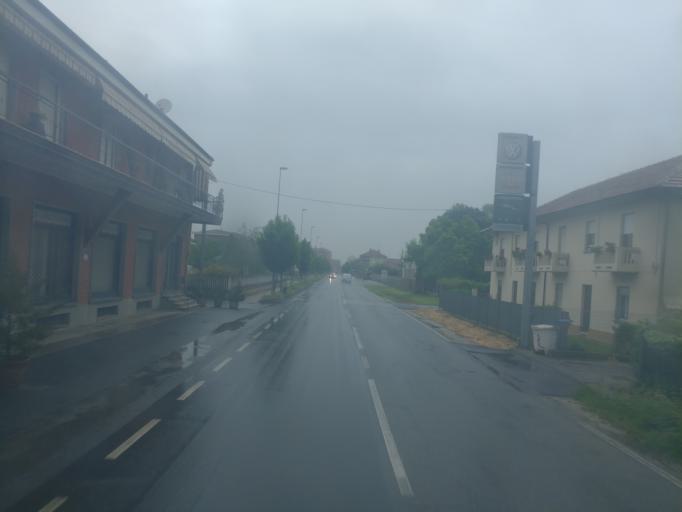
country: IT
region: Piedmont
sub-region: Provincia di Torino
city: La Loggia
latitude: 44.9493
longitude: 7.6692
